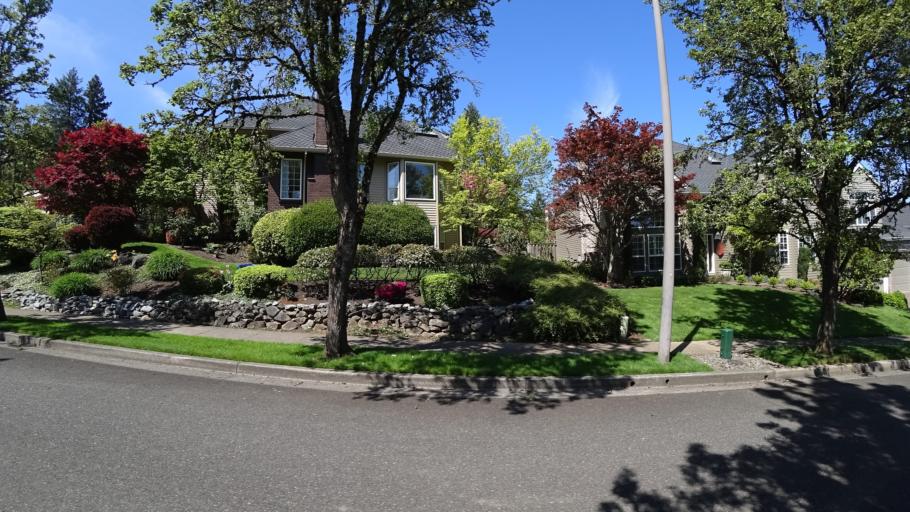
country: US
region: Oregon
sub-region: Washington County
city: King City
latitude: 45.4382
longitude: -122.8417
